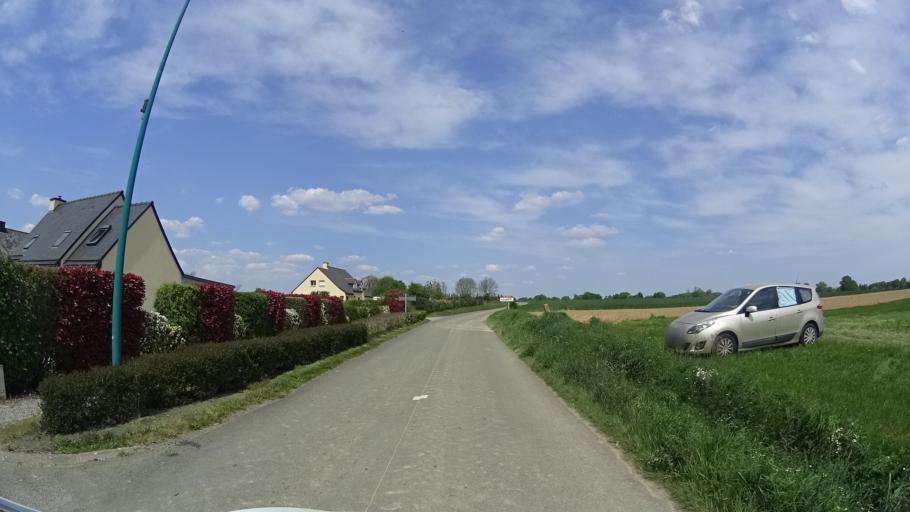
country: FR
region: Brittany
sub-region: Departement d'Ille-et-Vilaine
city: Torce
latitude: 48.0397
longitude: -1.2647
